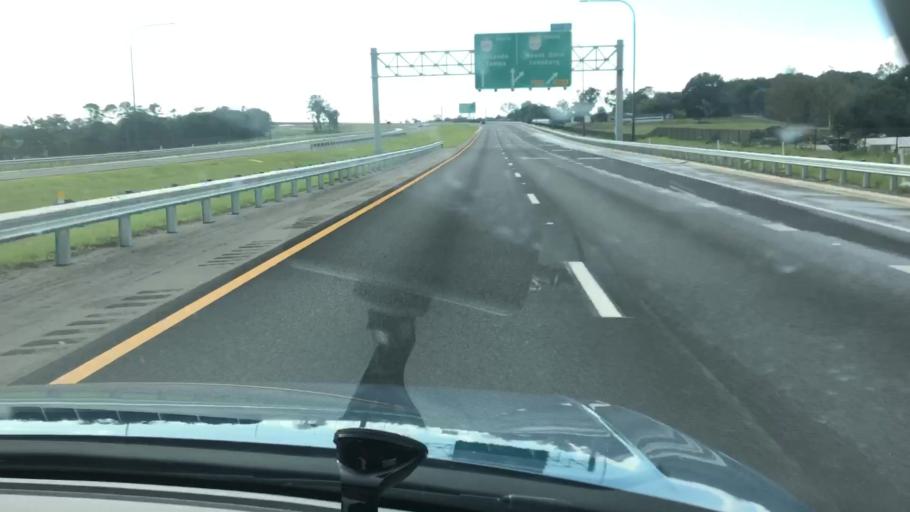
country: US
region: Florida
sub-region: Lake County
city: Mount Plymouth
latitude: 28.7758
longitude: -81.5506
